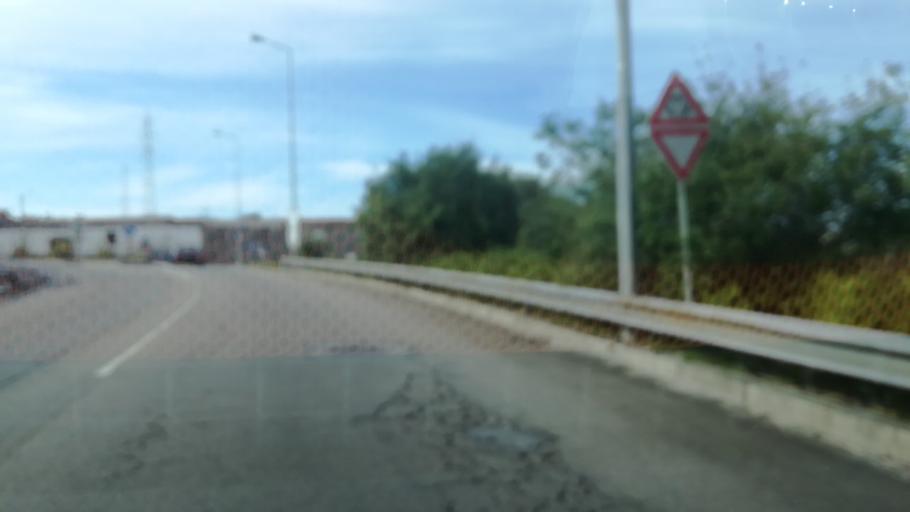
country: PT
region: Porto
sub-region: Valongo
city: Ermesinde
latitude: 41.2260
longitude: -8.5652
